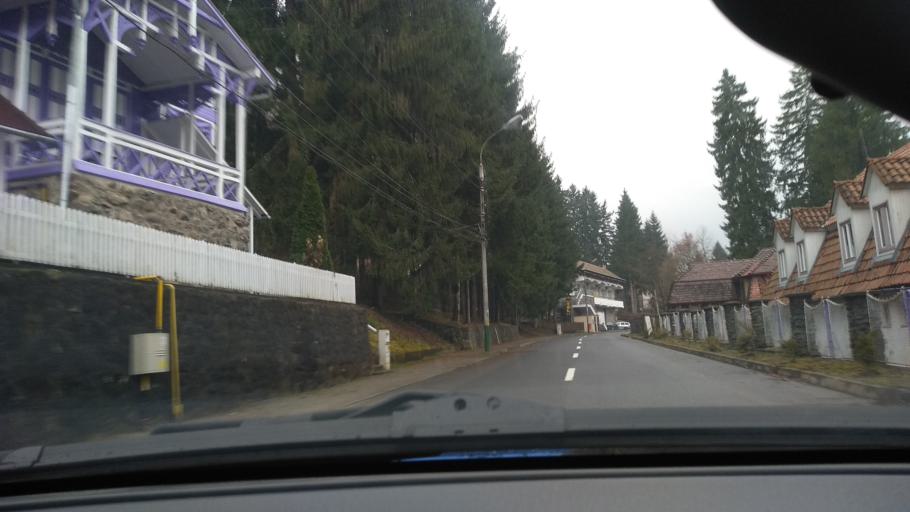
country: RO
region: Mures
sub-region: Oras Sovata
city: Sovata
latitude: 46.5978
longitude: 25.0848
